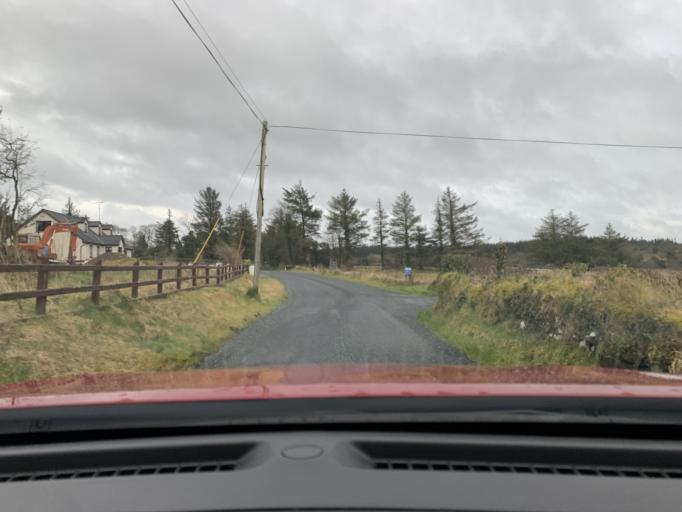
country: IE
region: Connaught
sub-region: Roscommon
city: Ballaghaderreen
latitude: 53.9664
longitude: -8.5145
